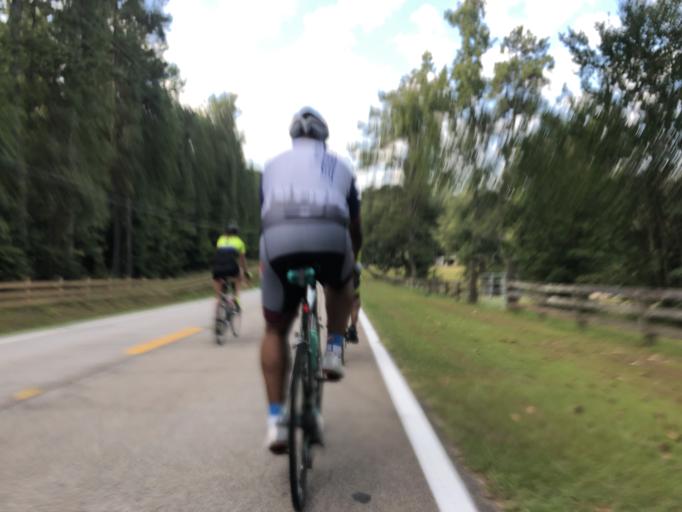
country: US
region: Georgia
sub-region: Fulton County
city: Palmetto
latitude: 33.5752
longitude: -84.6496
